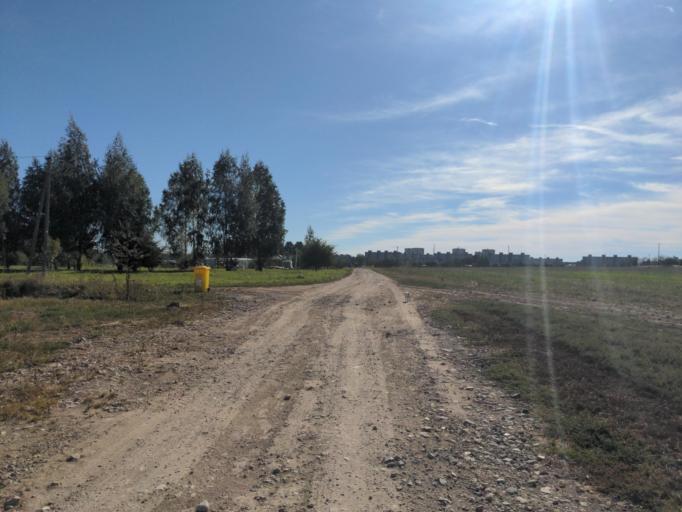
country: LT
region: Siauliu apskritis
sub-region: Siauliai
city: Siauliai
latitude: 55.9236
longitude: 23.2429
